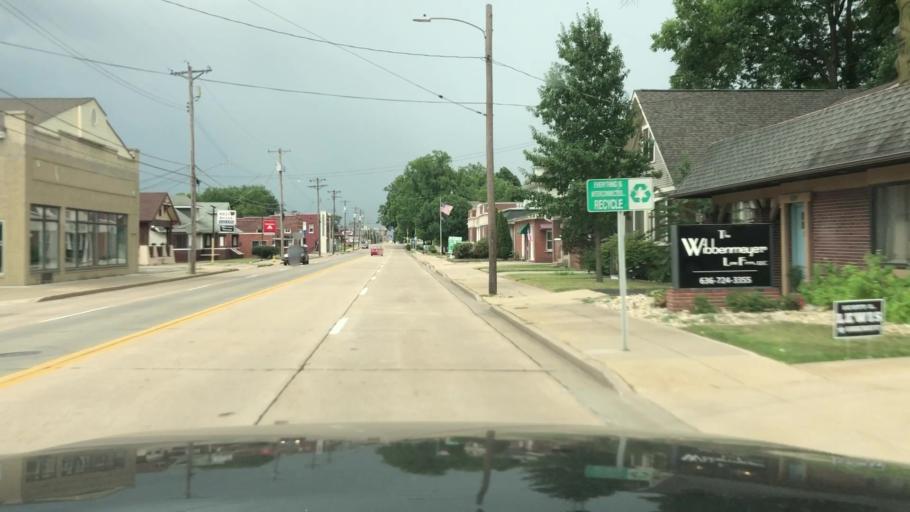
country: US
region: Missouri
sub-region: Saint Charles County
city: Saint Charles
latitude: 38.7838
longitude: -90.4954
